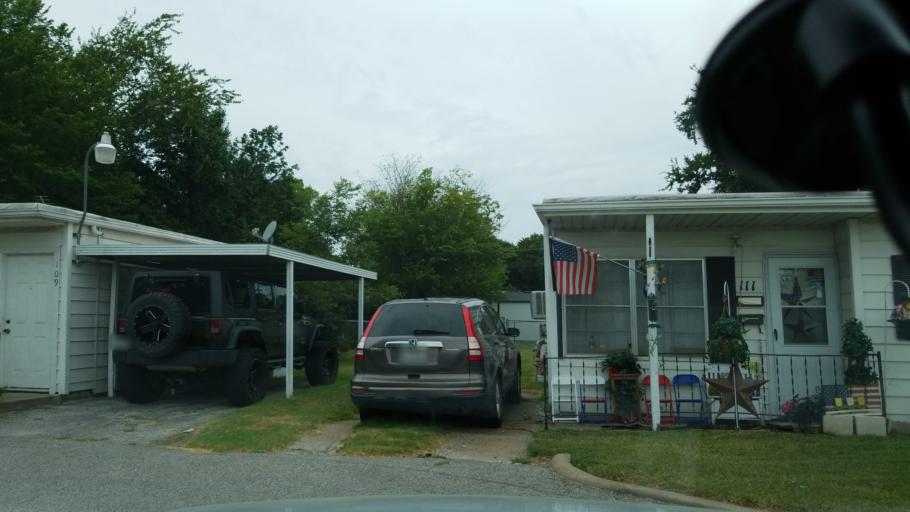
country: US
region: Texas
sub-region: Dallas County
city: Grand Prairie
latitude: 32.7359
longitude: -96.9930
